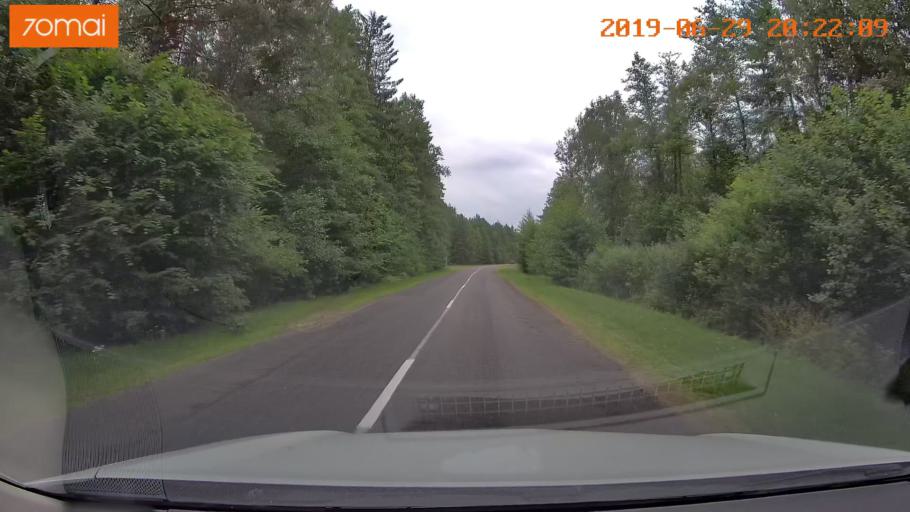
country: BY
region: Brest
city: Asnyezhytsy
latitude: 52.4284
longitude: 26.2536
